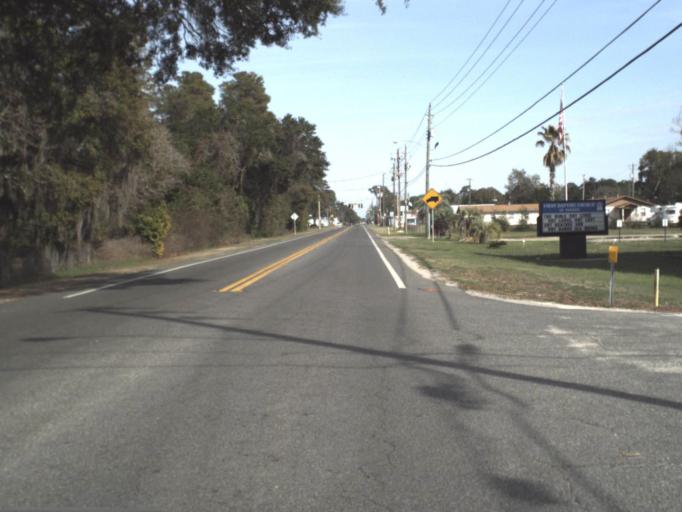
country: US
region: Florida
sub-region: Bay County
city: Parker
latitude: 30.1311
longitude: -85.6079
